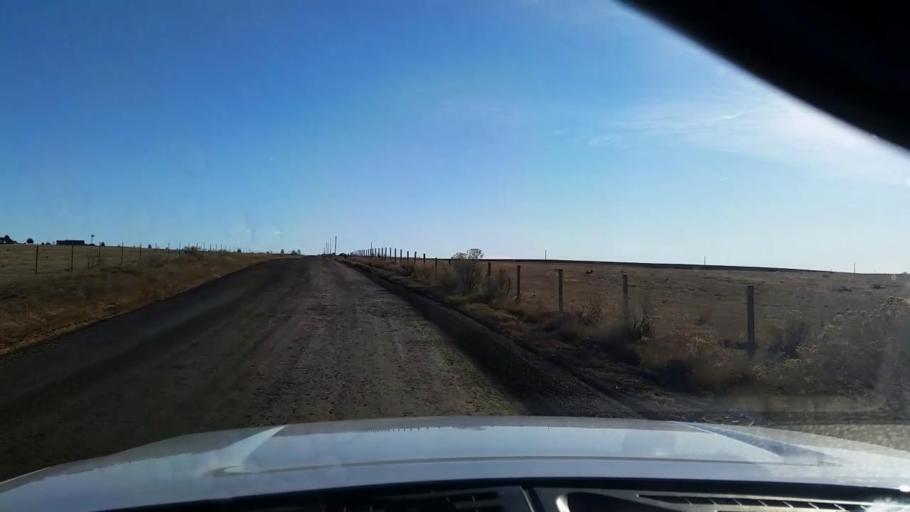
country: US
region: Colorado
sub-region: Larimer County
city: Wellington
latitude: 40.7696
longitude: -105.1147
